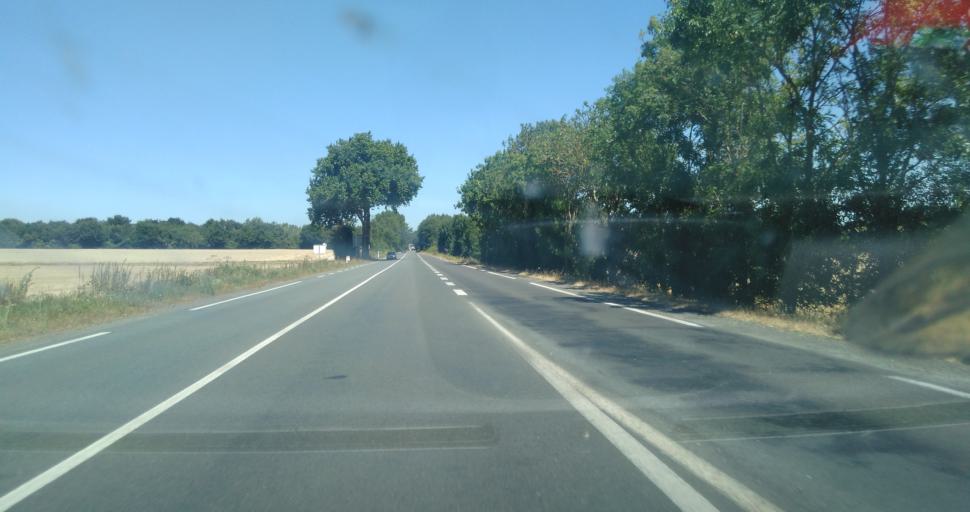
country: FR
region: Pays de la Loire
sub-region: Departement de la Vendee
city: Sainte-Hermine
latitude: 46.5714
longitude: -1.0532
